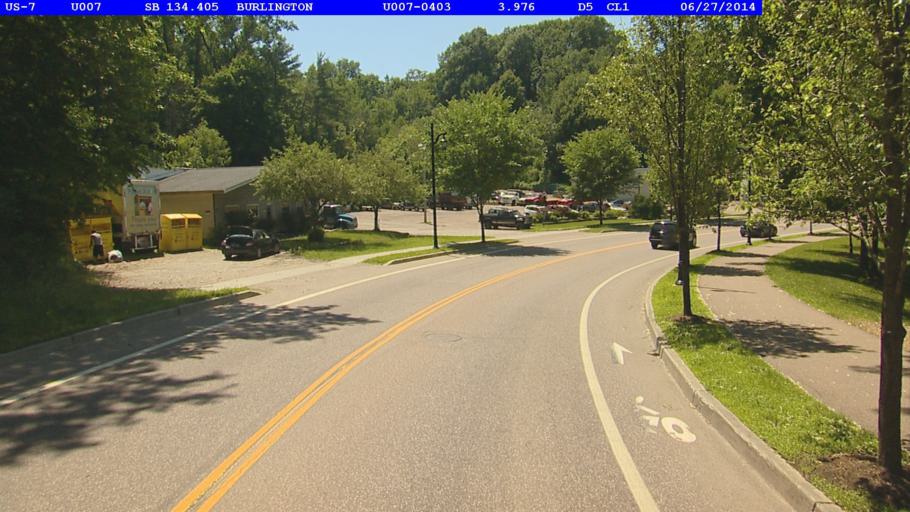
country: US
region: Vermont
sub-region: Chittenden County
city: Winooski
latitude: 44.4863
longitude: -73.1883
